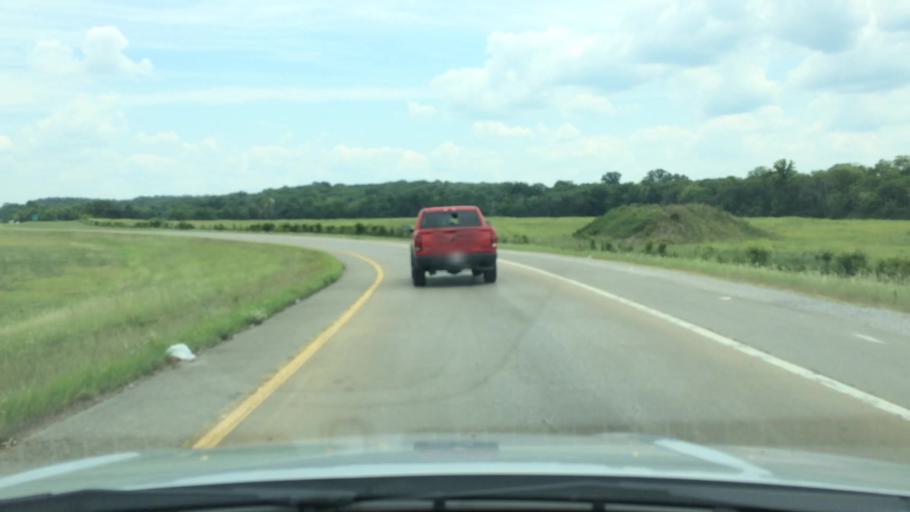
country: US
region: Tennessee
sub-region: Maury County
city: Spring Hill
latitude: 35.7327
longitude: -86.8932
